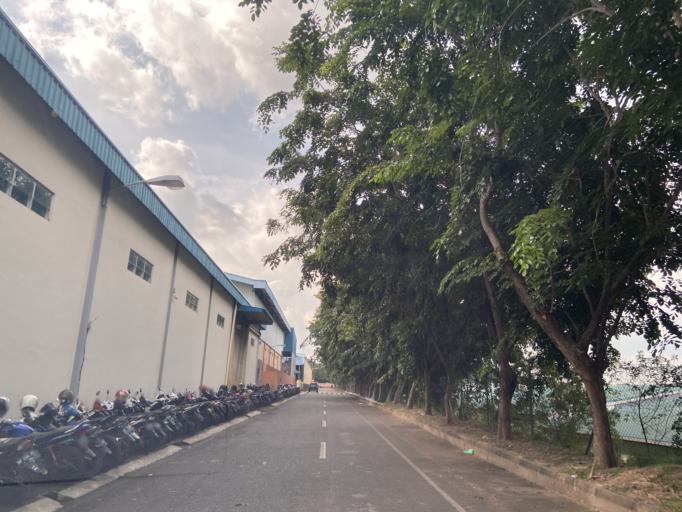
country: SG
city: Singapore
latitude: 1.1073
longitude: 104.0691
